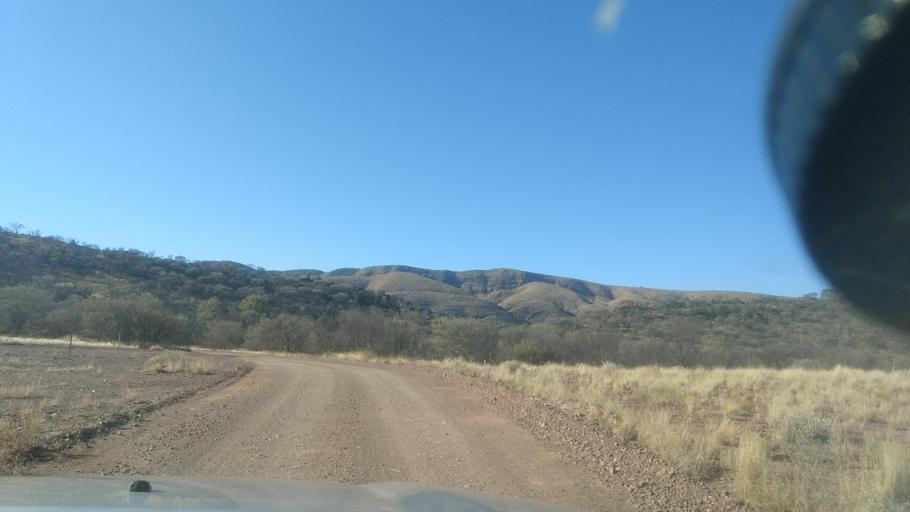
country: AU
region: Northern Territory
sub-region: Alice Springs
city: Alice Springs
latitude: -23.7501
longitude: 132.9160
